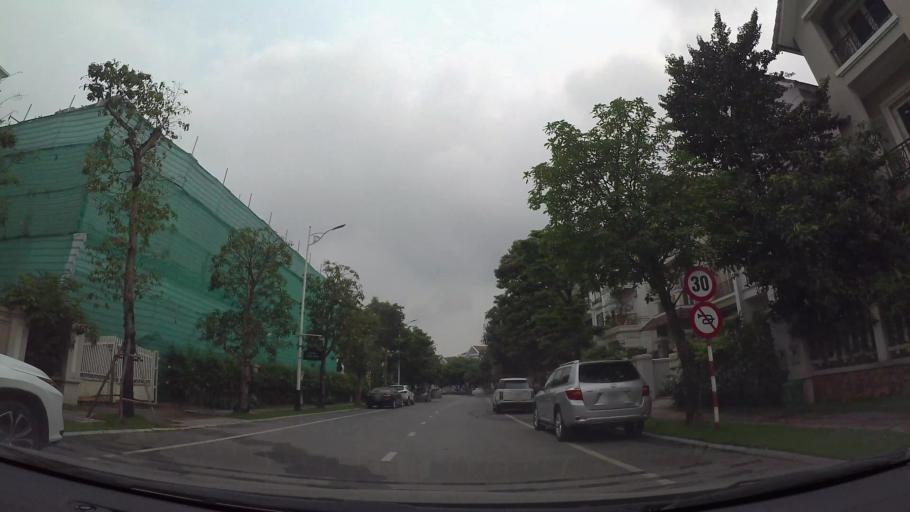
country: VN
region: Ha Noi
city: Trau Quy
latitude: 21.0400
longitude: 105.9204
